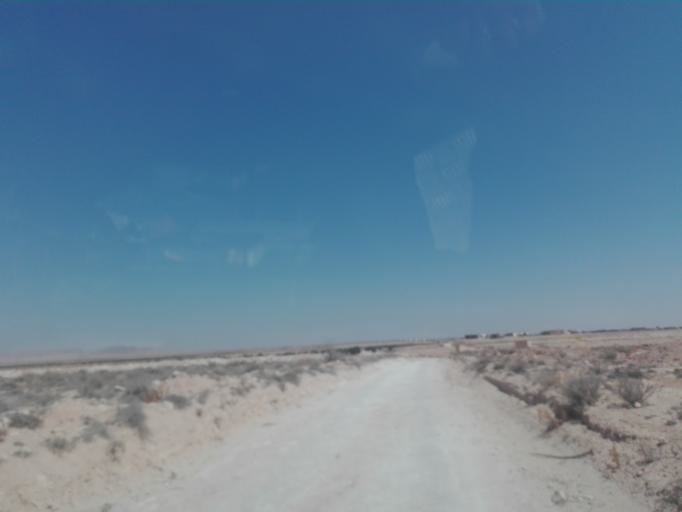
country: TN
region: Safaqis
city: Skhira
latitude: 34.3865
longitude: 9.9236
